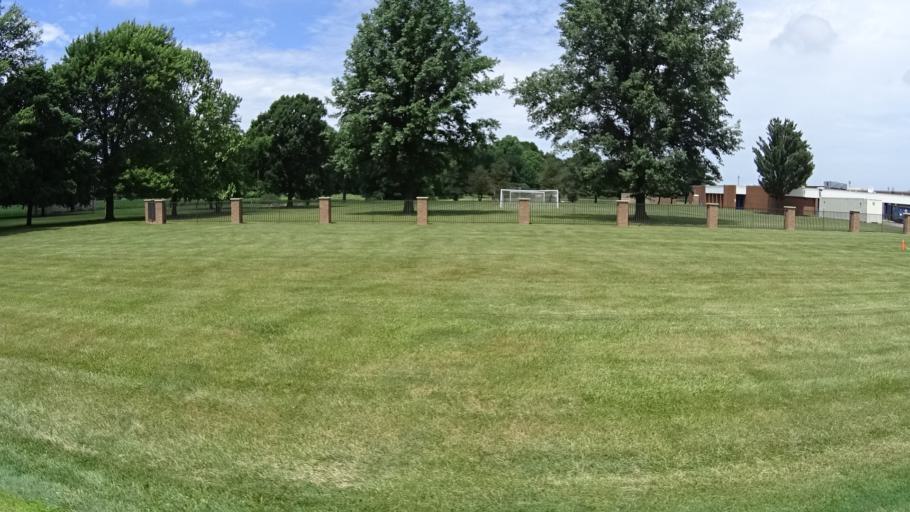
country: US
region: Ohio
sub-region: Erie County
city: Milan
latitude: 41.2984
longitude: -82.5754
